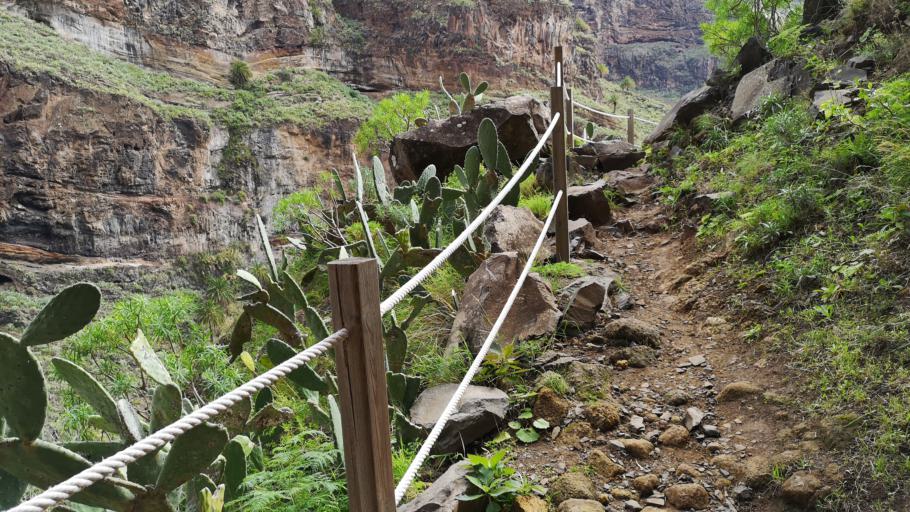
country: ES
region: Canary Islands
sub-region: Provincia de Santa Cruz de Tenerife
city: Alajero
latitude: 28.0768
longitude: -17.2294
